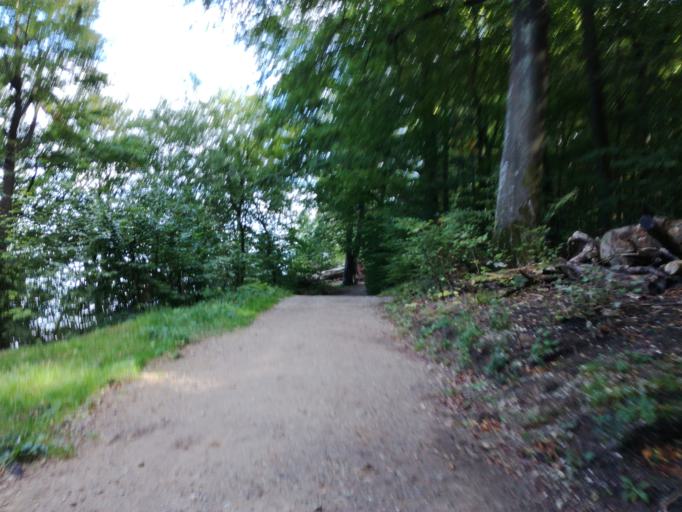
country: DK
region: South Denmark
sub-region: Fredericia Kommune
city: Snoghoj
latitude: 55.5100
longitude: 9.7159
